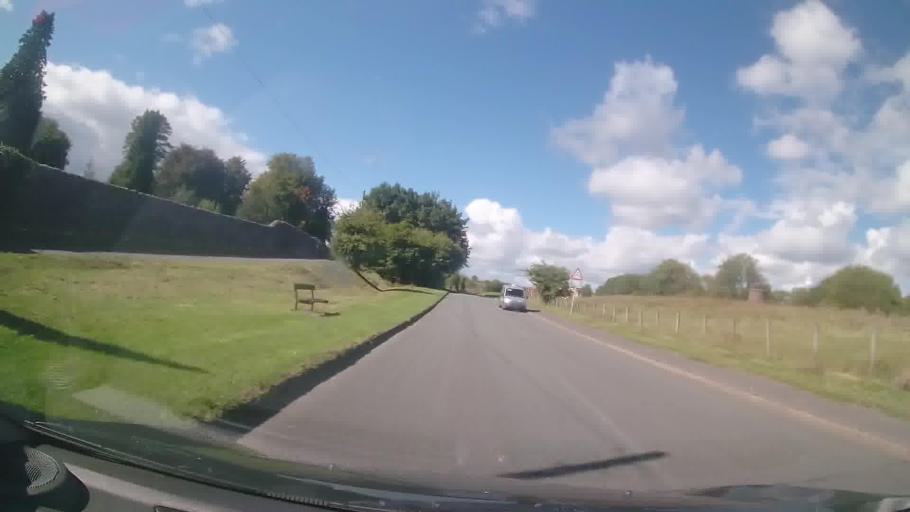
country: GB
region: Wales
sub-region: Merthyr Tydfil County Borough
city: Merthyr Tydfil
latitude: 51.7755
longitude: -3.3626
